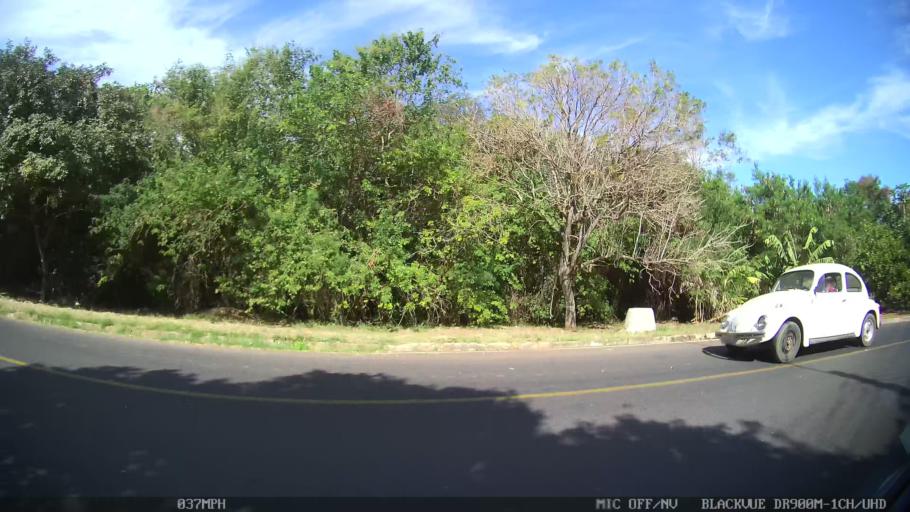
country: BR
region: Sao Paulo
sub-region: Sao Jose Do Rio Preto
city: Sao Jose do Rio Preto
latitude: -20.8503
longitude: -49.3646
